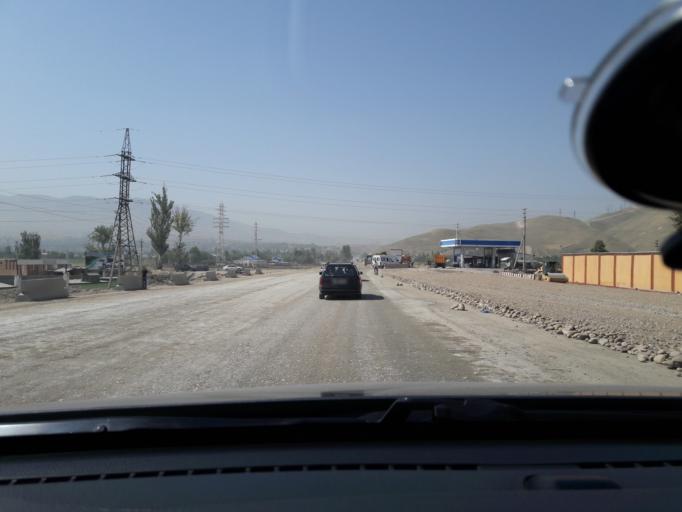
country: TJ
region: Dushanbe
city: Boshkengash
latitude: 38.4542
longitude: 68.7356
